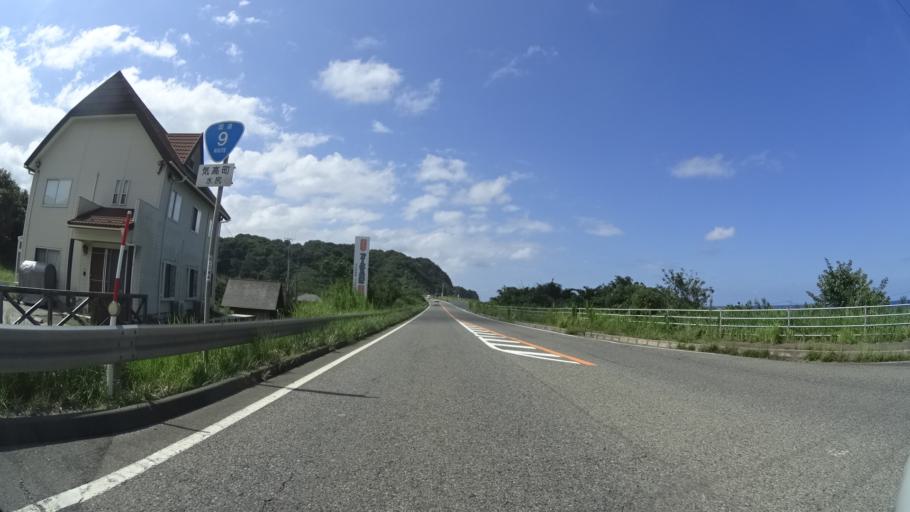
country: JP
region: Tottori
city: Tottori
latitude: 35.5224
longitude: 134.0976
